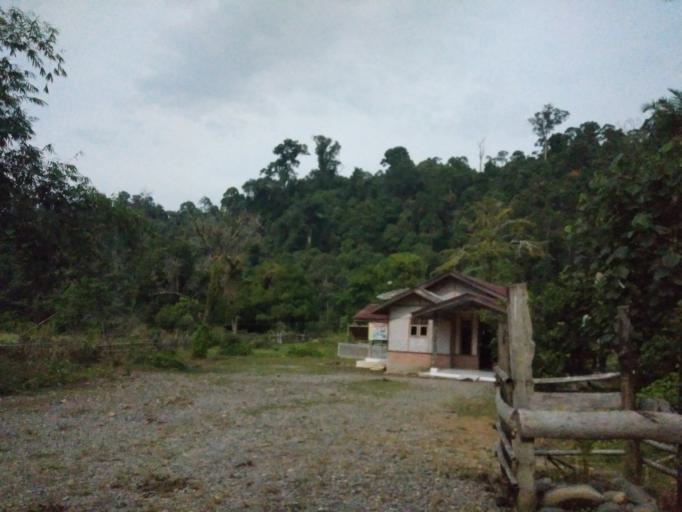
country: ID
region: Aceh
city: Tenggulun
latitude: 3.6961
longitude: 98.0705
